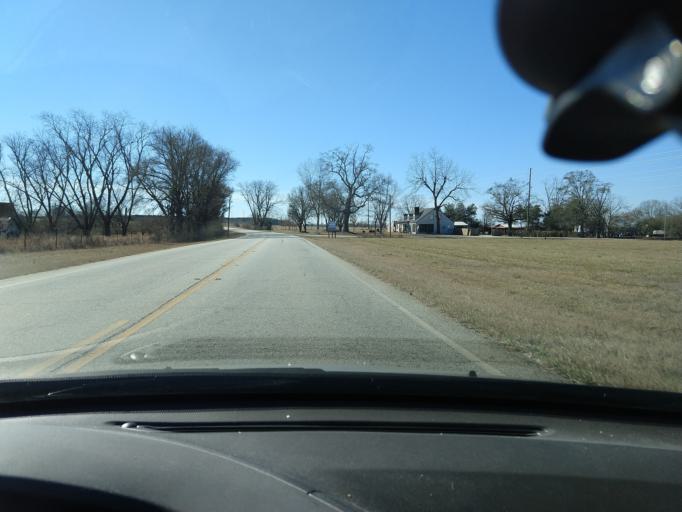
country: US
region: Georgia
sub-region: Newton County
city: Covington
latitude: 33.4883
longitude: -83.7419
